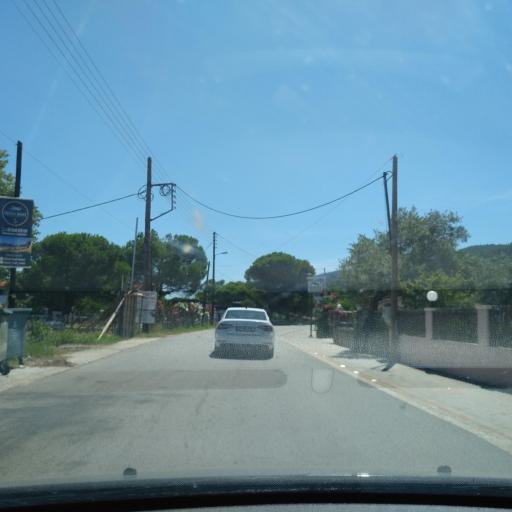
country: GR
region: Central Macedonia
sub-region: Nomos Chalkidikis
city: Neos Marmaras
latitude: 40.1893
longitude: 23.7774
